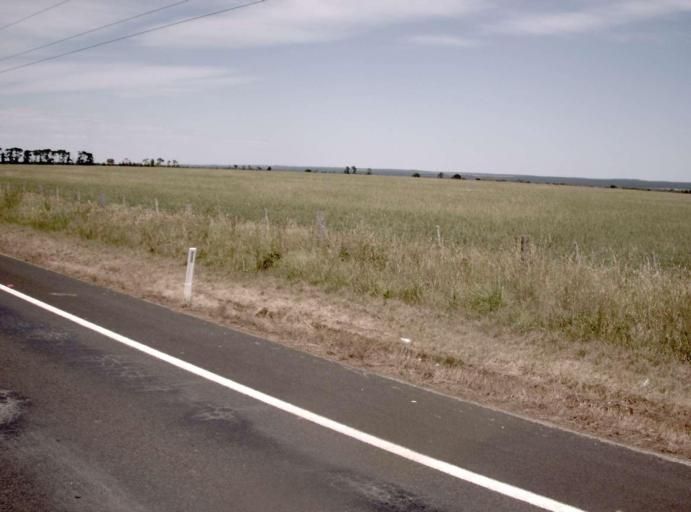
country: AU
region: Victoria
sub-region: Wellington
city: Sale
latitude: -38.1050
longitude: 146.9156
